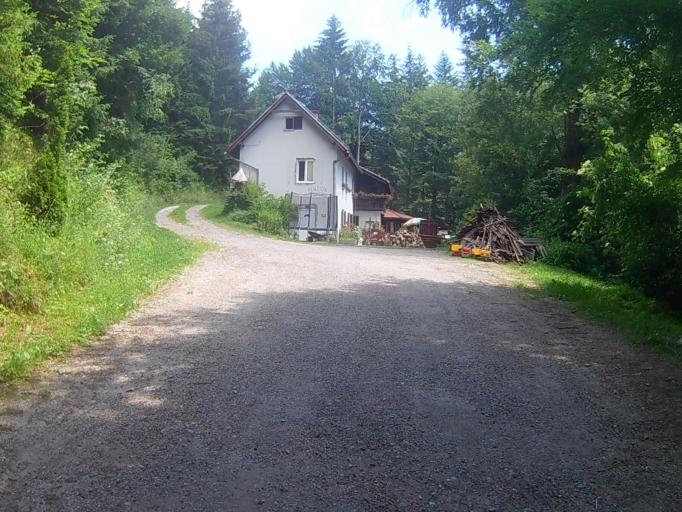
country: SI
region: Ruse
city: Bistrica ob Dravi
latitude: 46.5047
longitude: 15.5636
